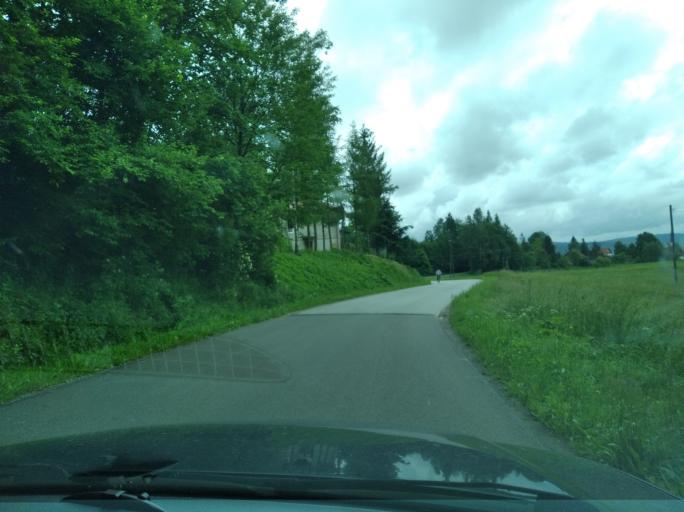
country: PL
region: Subcarpathian Voivodeship
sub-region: Powiat przemyski
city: Dubiecko
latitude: 49.8341
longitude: 22.3947
